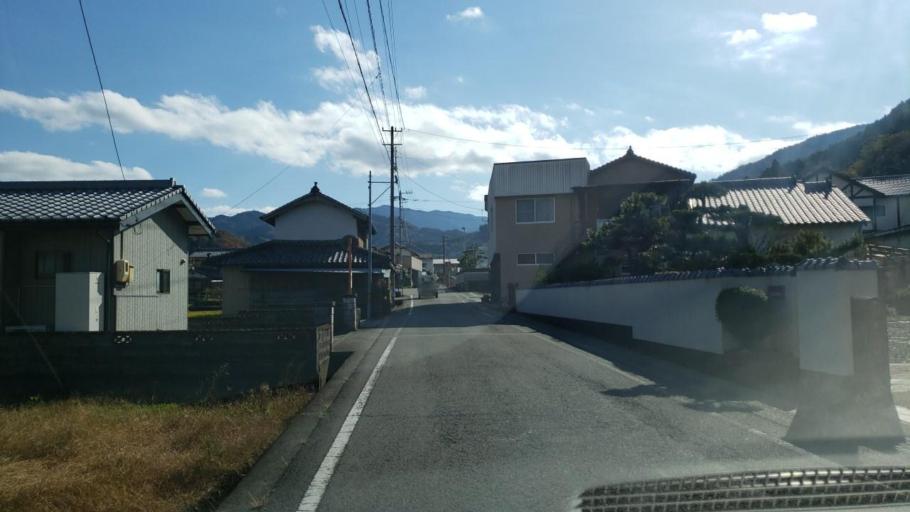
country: JP
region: Tokushima
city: Wakimachi
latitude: 34.0345
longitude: 134.0289
